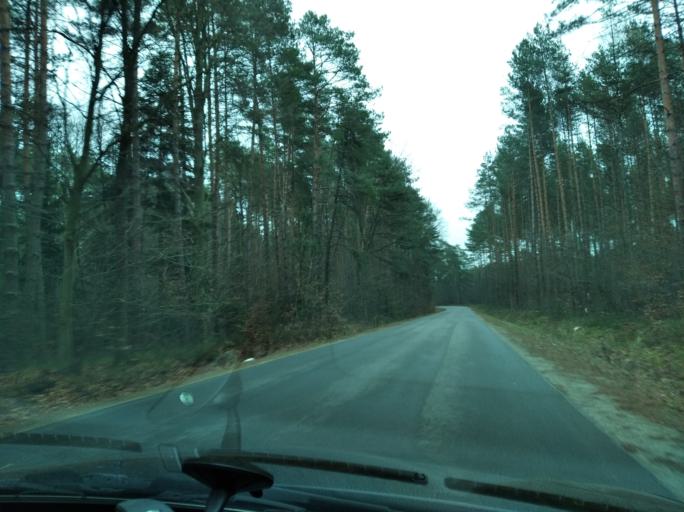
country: PL
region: Subcarpathian Voivodeship
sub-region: Powiat lancucki
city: Czarna
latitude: 50.1613
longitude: 22.1845
